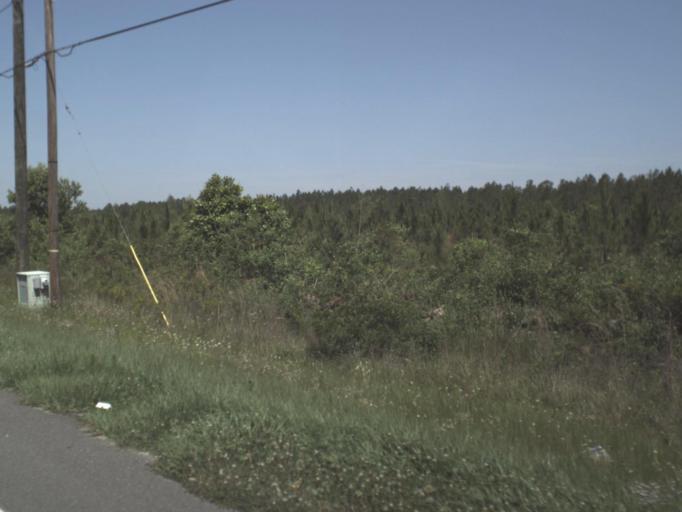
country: US
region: Florida
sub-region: Baker County
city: Macclenny
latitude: 30.2704
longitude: -82.1903
